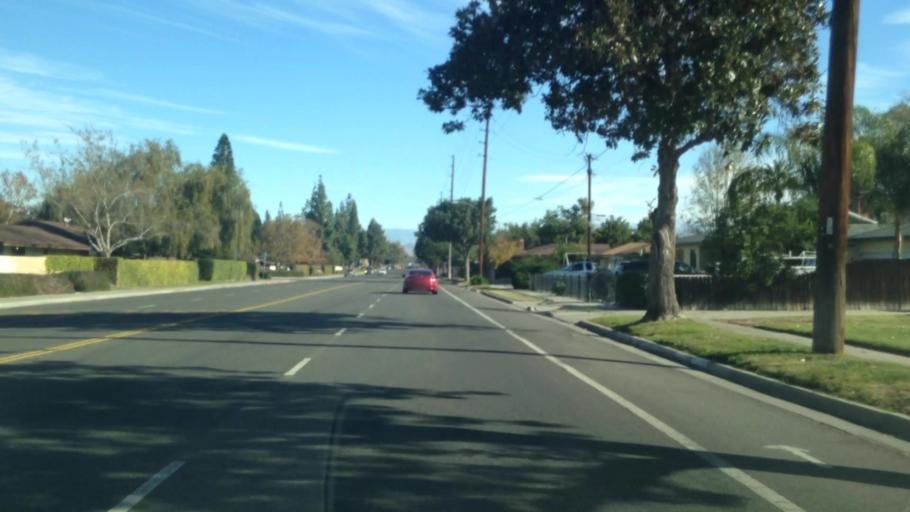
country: US
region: California
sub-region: Riverside County
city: Pedley
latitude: 33.9283
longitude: -117.4487
